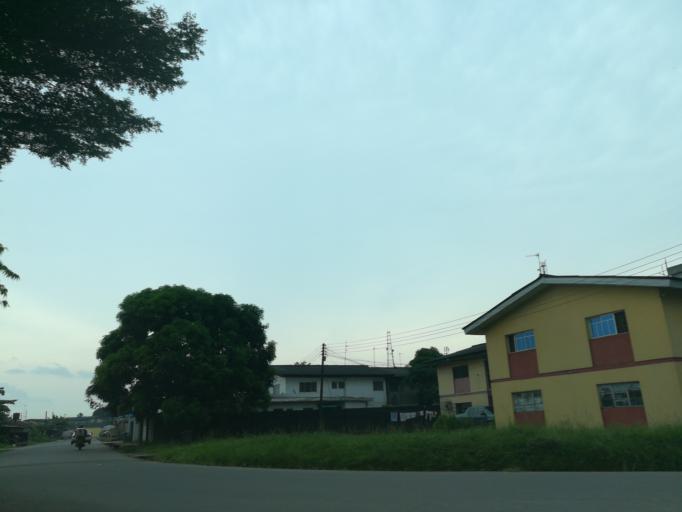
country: NG
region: Rivers
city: Port Harcourt
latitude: 4.8211
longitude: 7.0277
